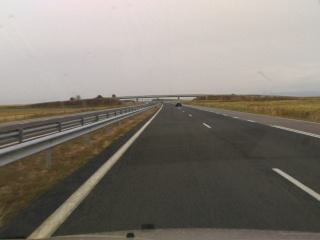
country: BG
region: Stara Zagora
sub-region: Obshtina Radnevo
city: Radnevo
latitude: 42.3930
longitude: 25.8907
